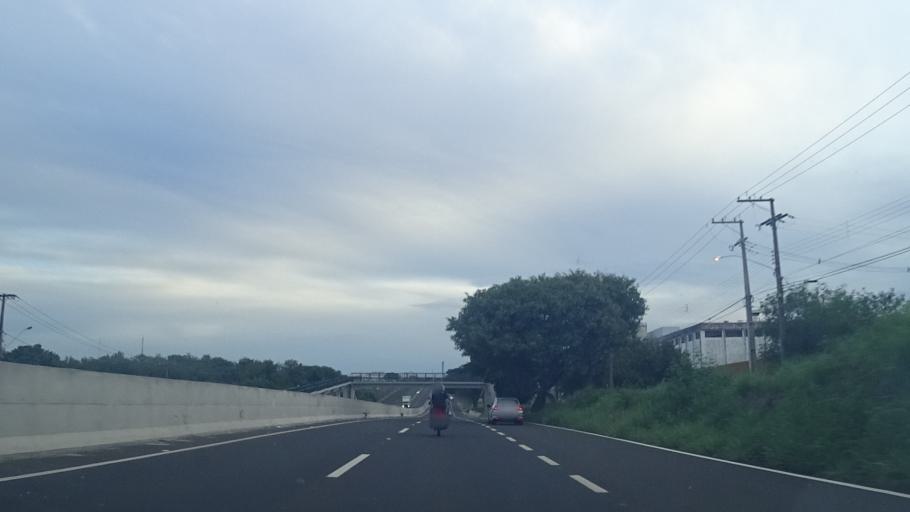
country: BR
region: Sao Paulo
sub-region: Presidente Prudente
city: Presidente Prudente
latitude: -22.1576
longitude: -51.3934
